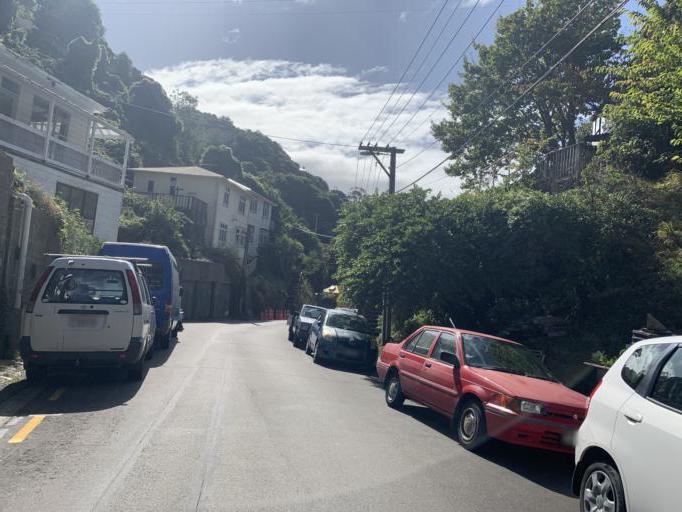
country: NZ
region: Wellington
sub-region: Wellington City
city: Kelburn
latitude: -41.2953
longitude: 174.7584
